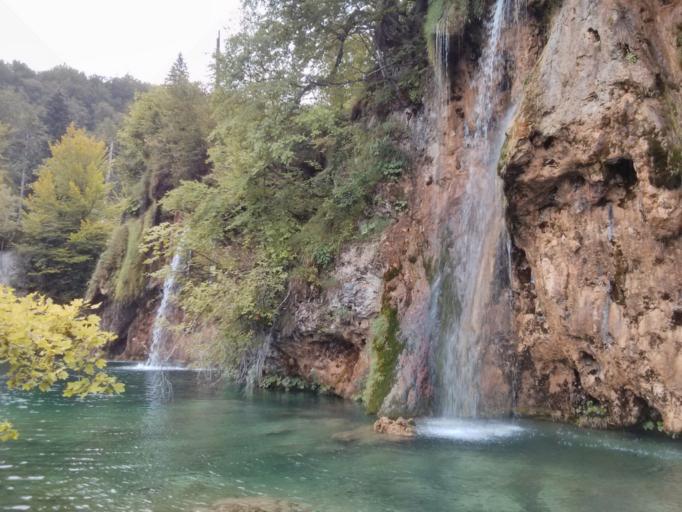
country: HR
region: Licko-Senjska
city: Jezerce
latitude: 44.8768
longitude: 15.6086
